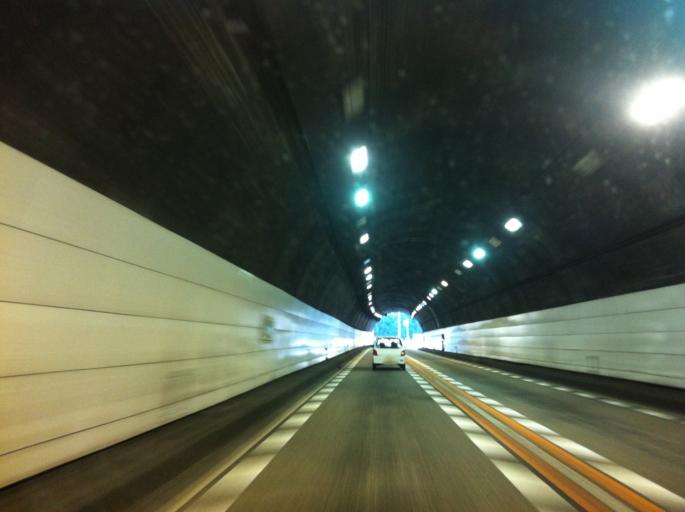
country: JP
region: Shizuoka
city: Kanaya
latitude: 34.8247
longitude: 138.1212
